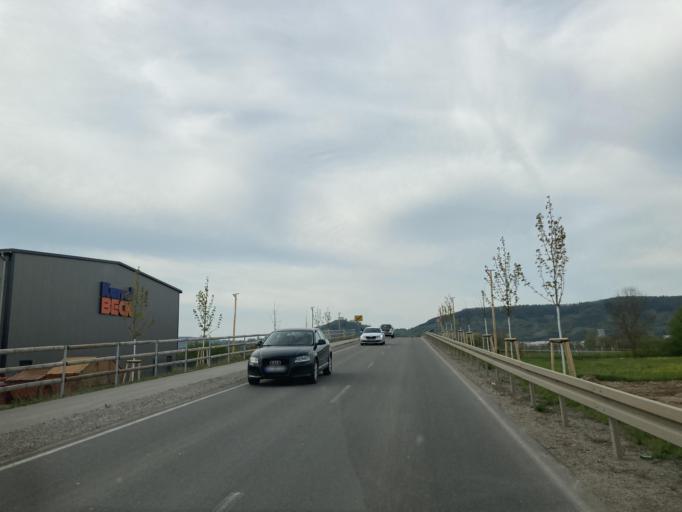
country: DE
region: Baden-Wuerttemberg
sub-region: Tuebingen Region
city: Tuebingen
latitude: 48.4862
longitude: 9.0007
